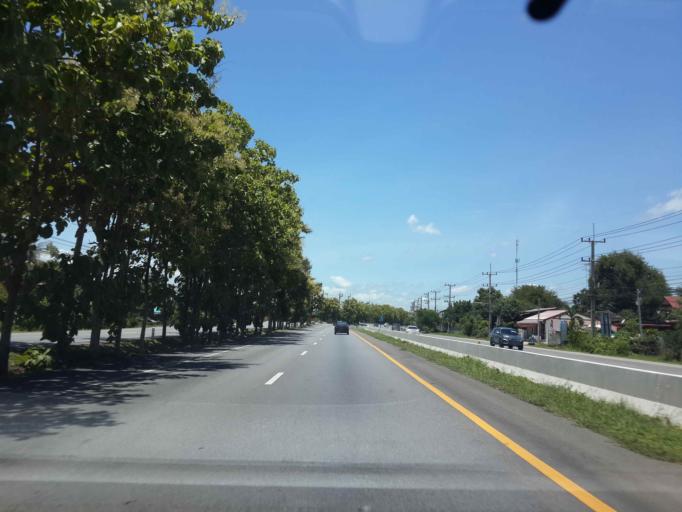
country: TH
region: Phetchaburi
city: Khao Yoi
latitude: 13.1622
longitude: 99.8441
